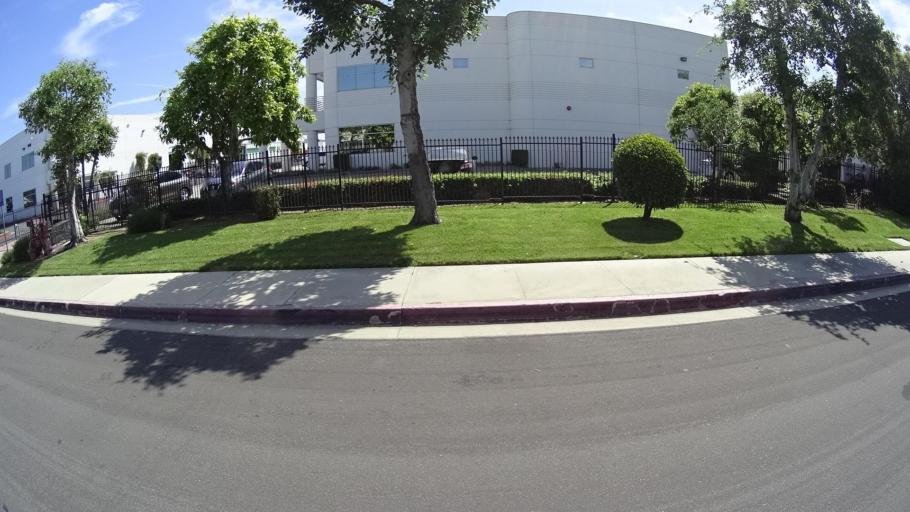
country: US
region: California
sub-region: Los Angeles County
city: South San Jose Hills
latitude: 34.0026
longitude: -117.9211
